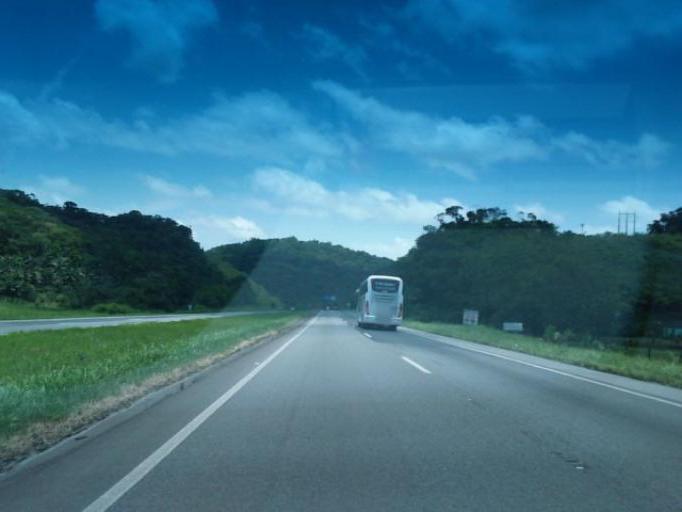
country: BR
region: Sao Paulo
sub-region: Juquia
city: Juquia
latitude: -24.3777
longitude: -47.7104
